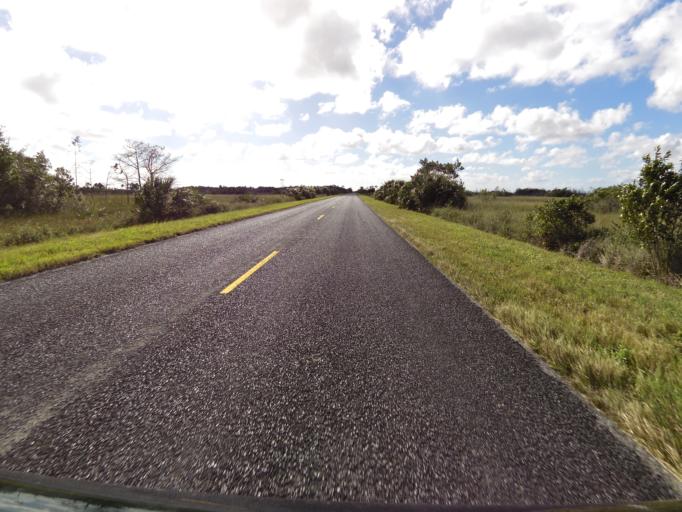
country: US
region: Florida
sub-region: Miami-Dade County
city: Florida City
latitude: 25.3984
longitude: -80.7948
